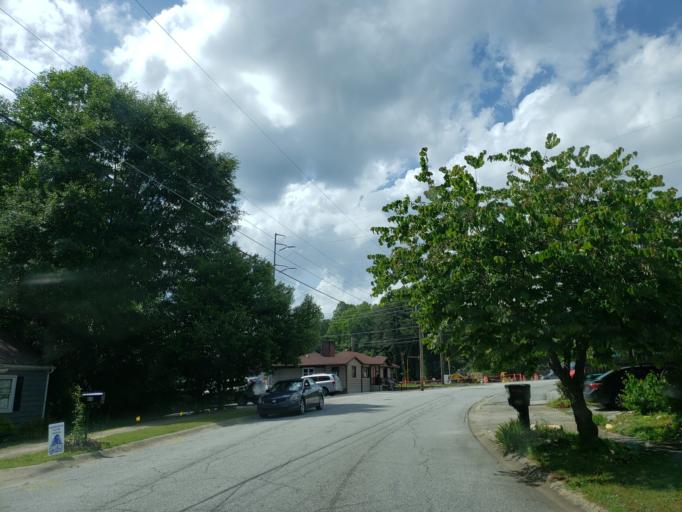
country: US
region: Georgia
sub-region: Cobb County
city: Smyrna
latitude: 33.8938
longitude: -84.5352
